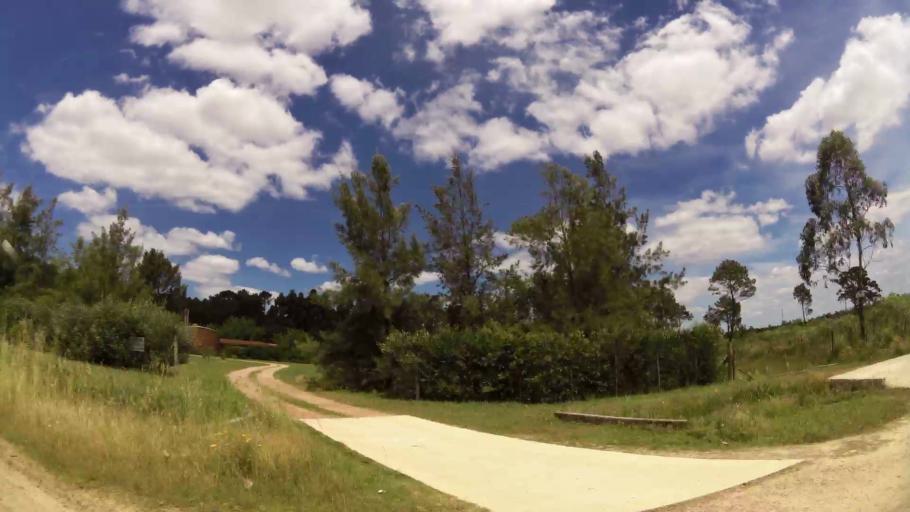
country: UY
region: Canelones
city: Pando
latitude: -34.8030
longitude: -55.9491
